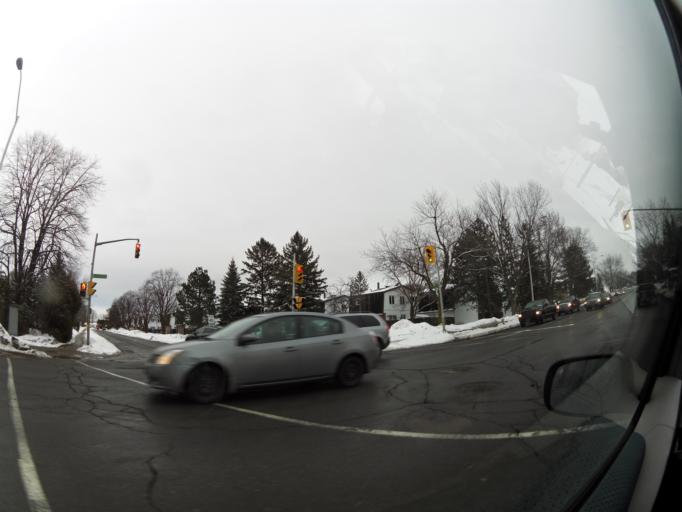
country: CA
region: Quebec
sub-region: Outaouais
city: Gatineau
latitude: 45.4517
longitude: -75.5966
